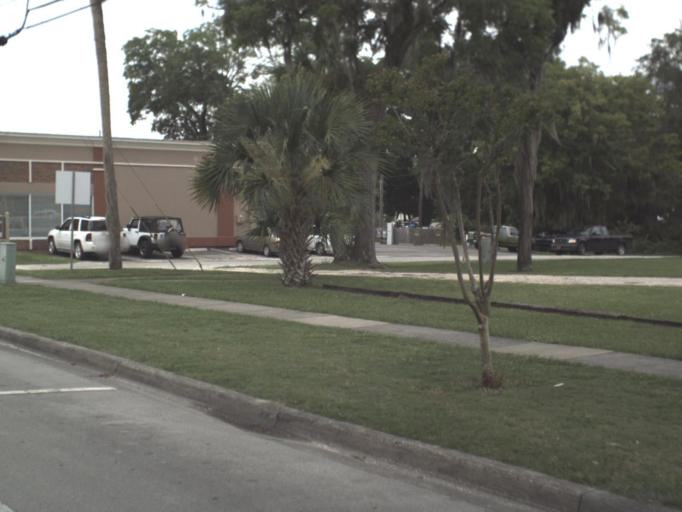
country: US
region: Florida
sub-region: Alachua County
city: High Springs
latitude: 29.8281
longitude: -82.5963
